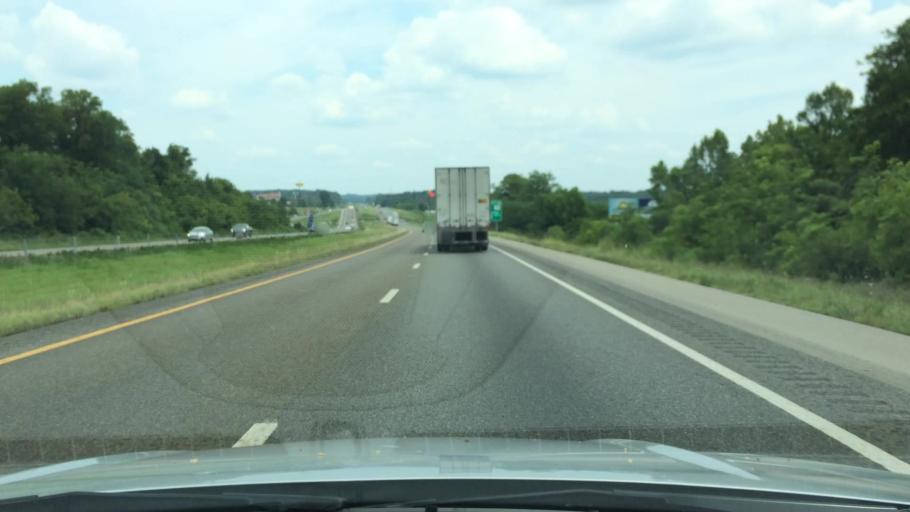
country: US
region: Tennessee
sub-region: Maury County
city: Spring Hill
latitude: 35.6375
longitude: -86.8942
